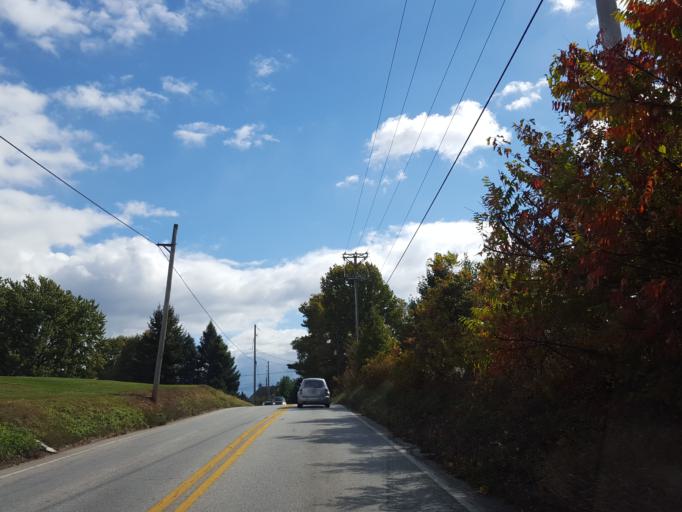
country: US
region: Pennsylvania
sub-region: York County
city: Spry
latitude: 39.9328
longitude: -76.6756
